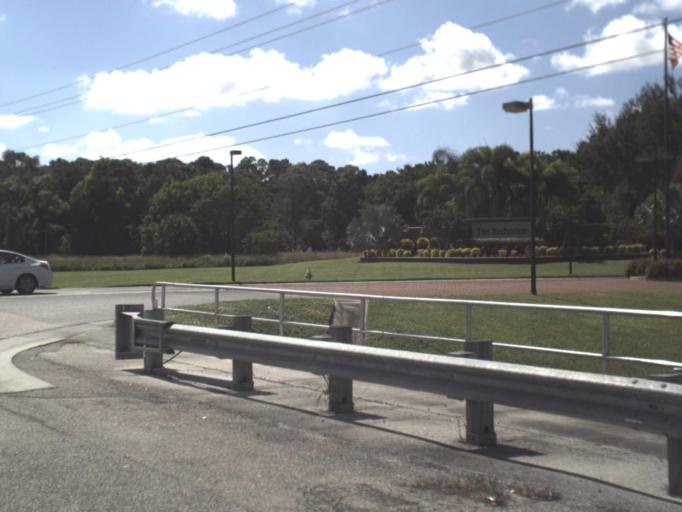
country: US
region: Florida
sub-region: Lee County
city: San Carlos Park
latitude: 26.4817
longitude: -81.8398
